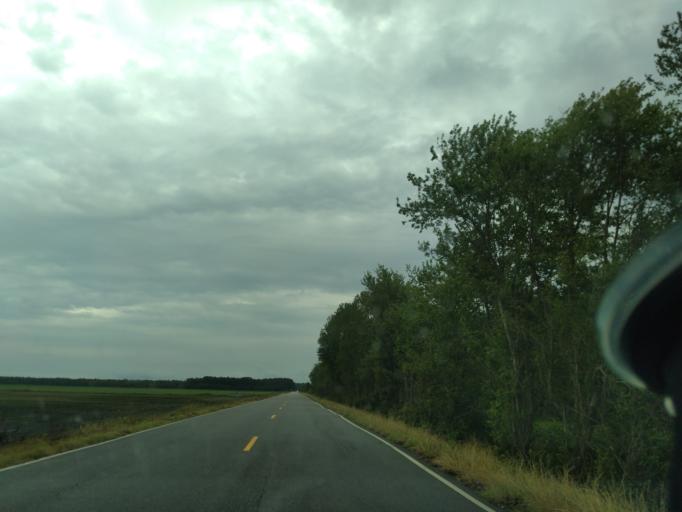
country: US
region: North Carolina
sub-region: Washington County
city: Plymouth
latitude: 35.8357
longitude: -76.5335
